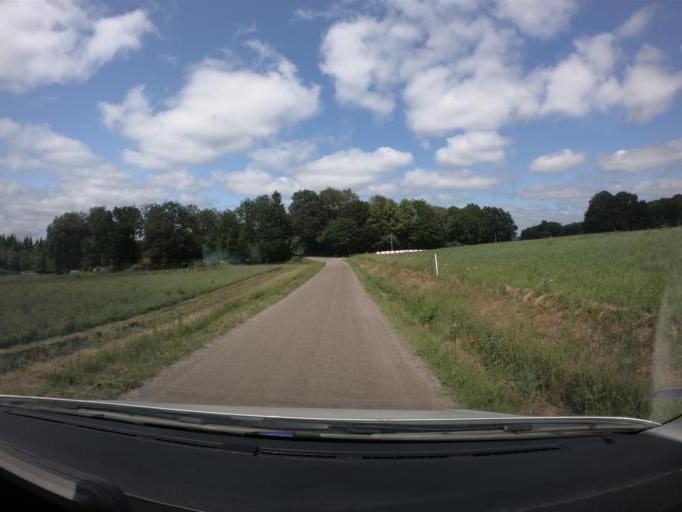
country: SE
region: Skane
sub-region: Hassleholms Kommun
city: Sosdala
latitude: 55.9765
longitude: 13.6483
